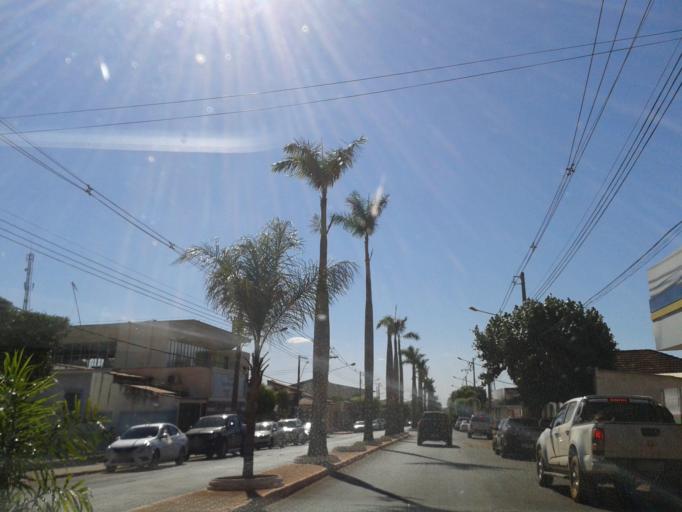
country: BR
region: Minas Gerais
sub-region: Centralina
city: Centralina
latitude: -18.5894
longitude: -49.1971
